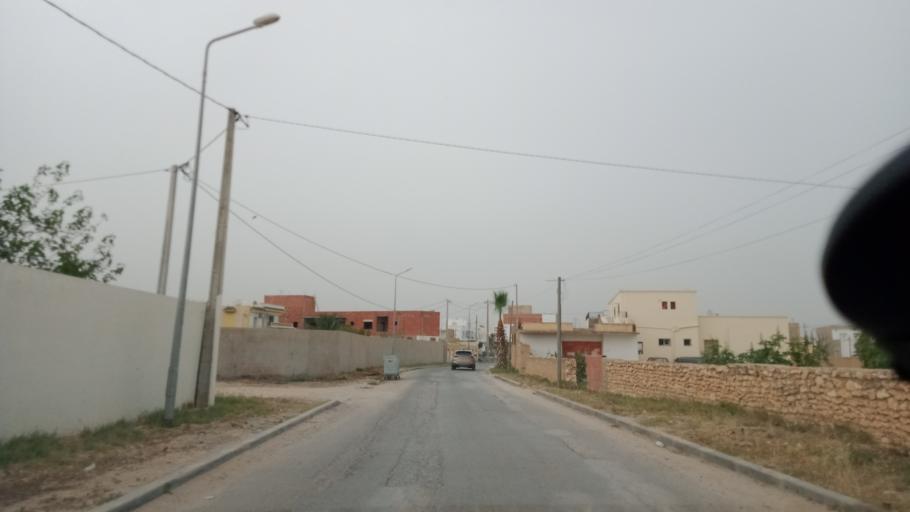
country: TN
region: Safaqis
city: Al Qarmadah
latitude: 34.7950
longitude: 10.7716
